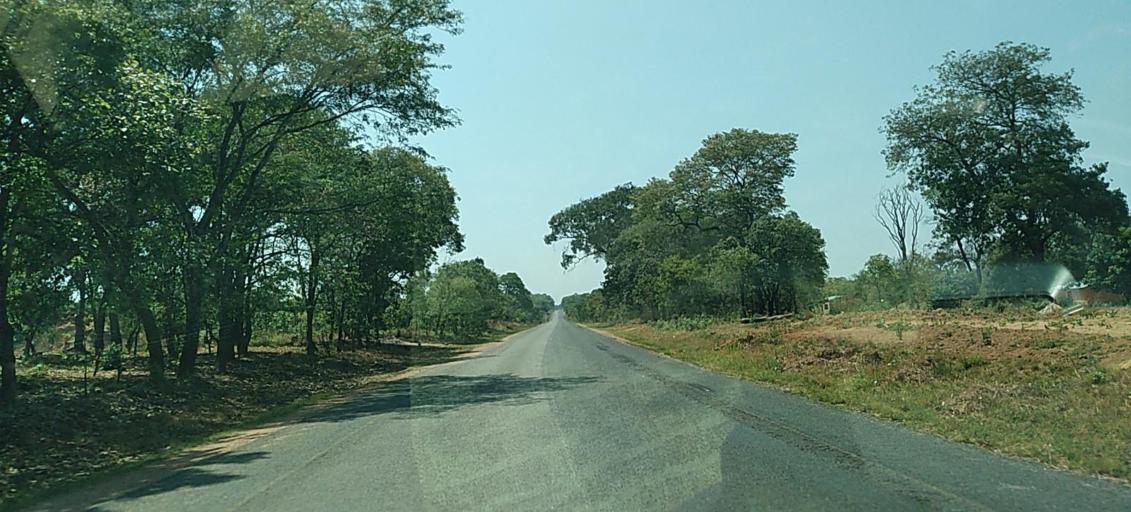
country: ZM
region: North-Western
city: Solwezi
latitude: -12.2905
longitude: 25.8113
